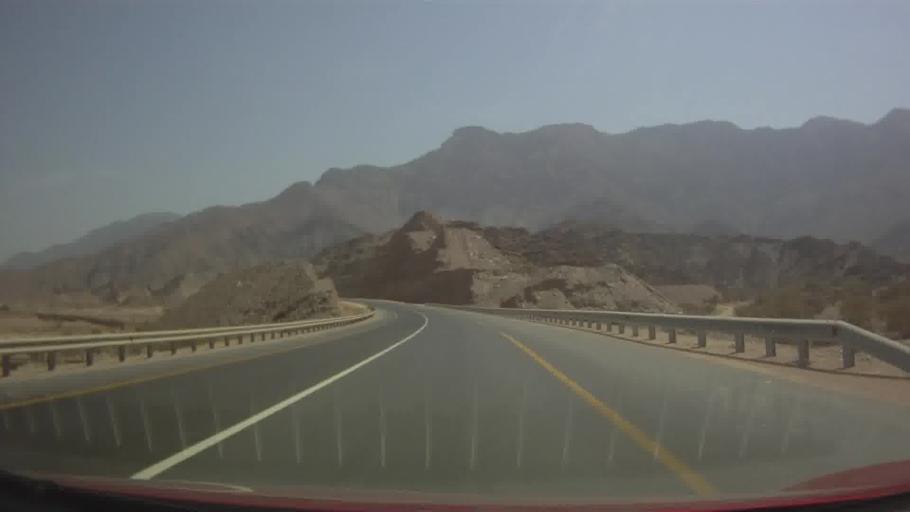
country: OM
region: Muhafazat Masqat
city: Muscat
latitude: 23.4009
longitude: 58.7816
